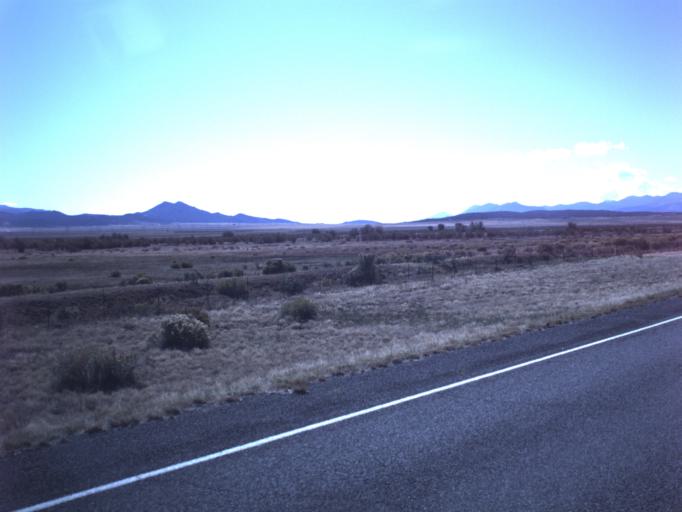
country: US
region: Utah
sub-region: Juab County
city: Nephi
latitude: 39.5151
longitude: -111.9441
